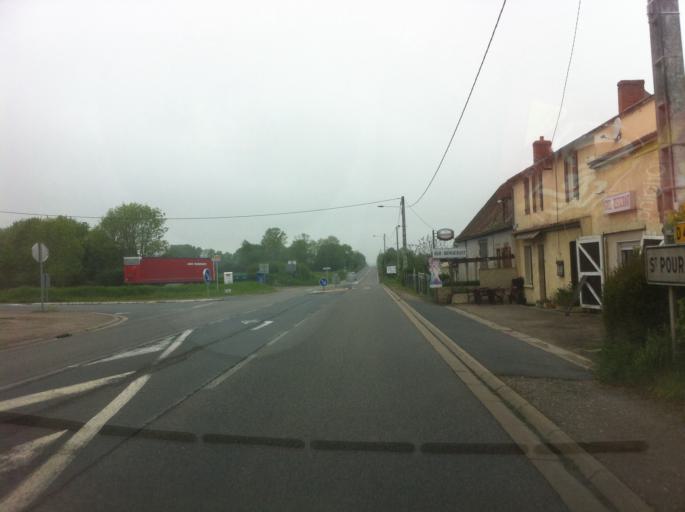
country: FR
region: Auvergne
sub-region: Departement de l'Allier
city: Montmarault
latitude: 46.3254
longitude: 3.0620
